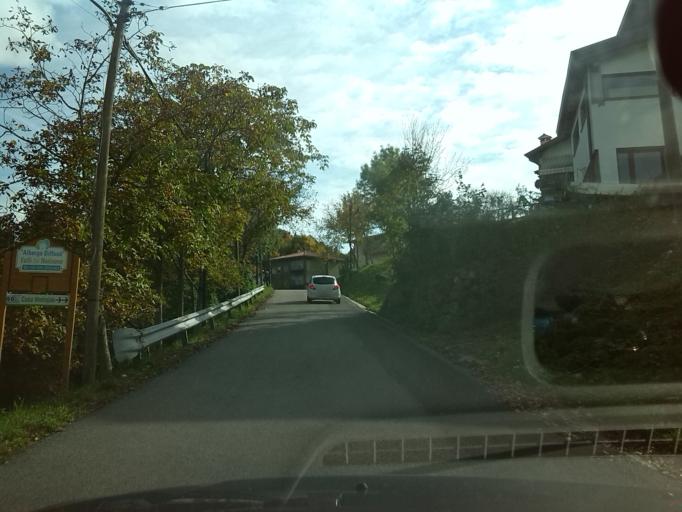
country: IT
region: Friuli Venezia Giulia
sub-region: Provincia di Udine
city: Stregna
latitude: 46.1262
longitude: 13.5953
